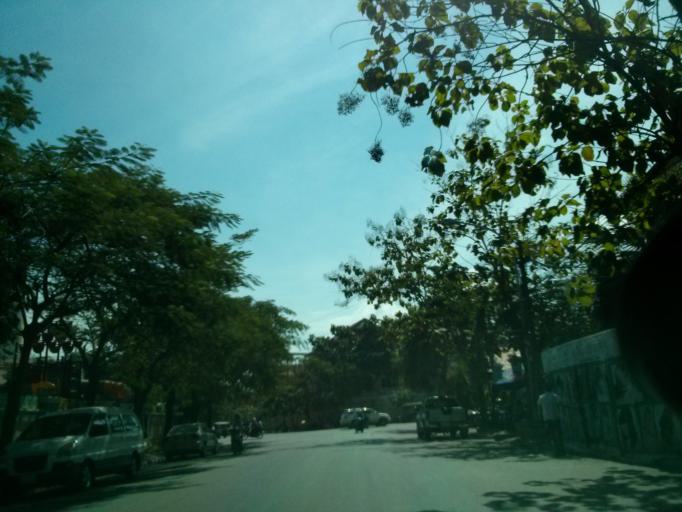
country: KH
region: Phnom Penh
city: Phnom Penh
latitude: 11.5792
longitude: 104.8941
